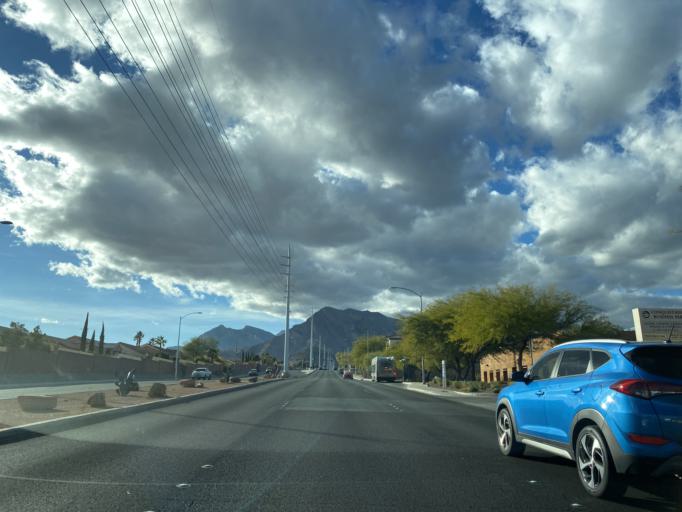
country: US
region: Nevada
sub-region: Clark County
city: Summerlin South
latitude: 36.2184
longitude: -115.3117
